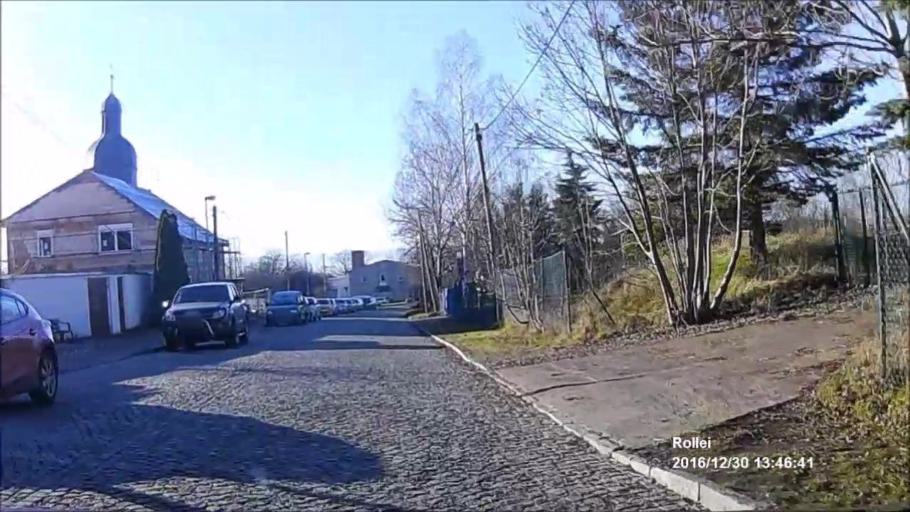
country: DE
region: Thuringia
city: Rockhausen
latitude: 50.9191
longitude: 11.0563
